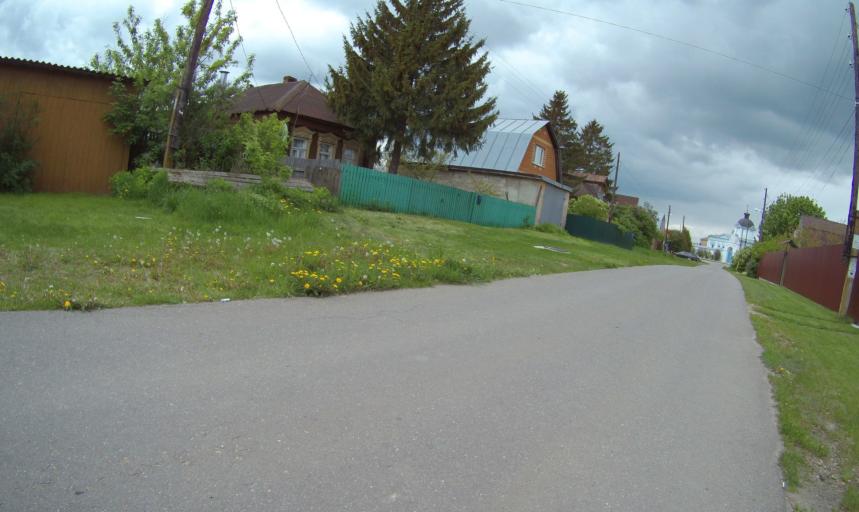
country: RU
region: Moskovskaya
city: Raduzhnyy
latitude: 55.1178
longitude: 38.7627
